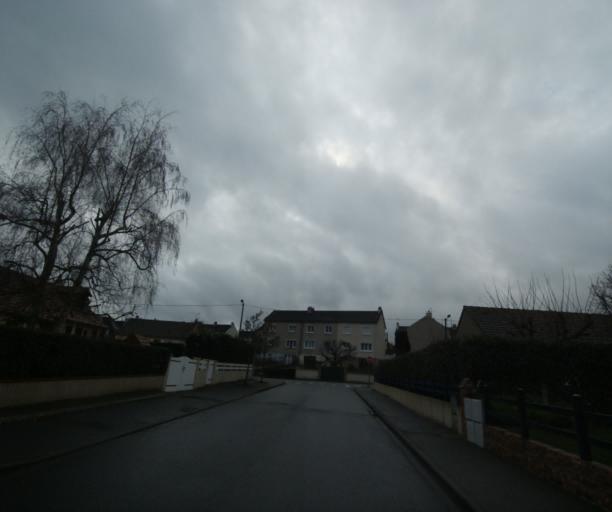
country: FR
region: Pays de la Loire
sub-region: Departement de la Sarthe
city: Coulaines
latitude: 48.0262
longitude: 0.1872
